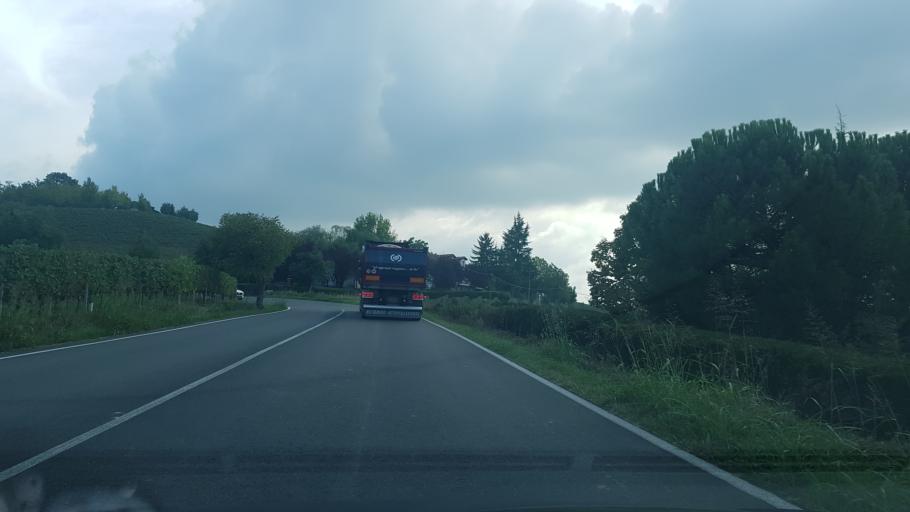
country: IT
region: Piedmont
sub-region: Provincia di Asti
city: Castelnuovo Belbo
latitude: 44.7779
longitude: 8.3943
